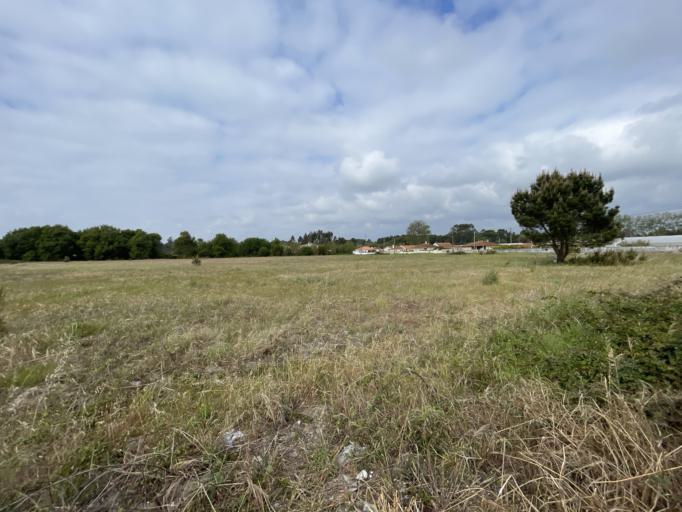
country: PT
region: Aveiro
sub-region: Ovar
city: Ovar
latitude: 40.8663
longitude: -8.6590
